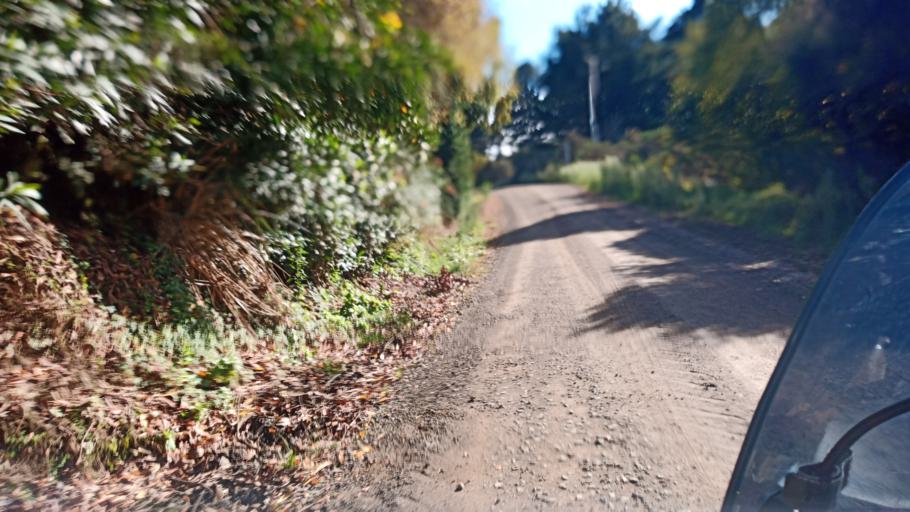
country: NZ
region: Bay of Plenty
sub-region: Opotiki District
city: Opotiki
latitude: -38.4733
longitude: 177.4393
